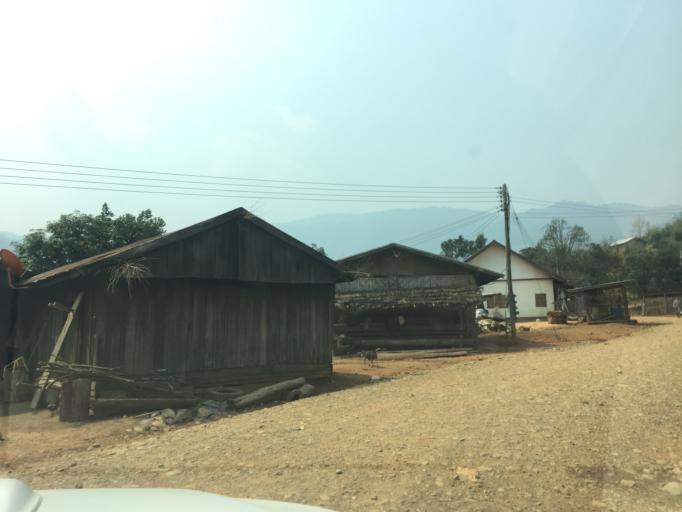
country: TH
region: Phayao
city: Phu Sang
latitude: 19.5669
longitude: 100.5265
